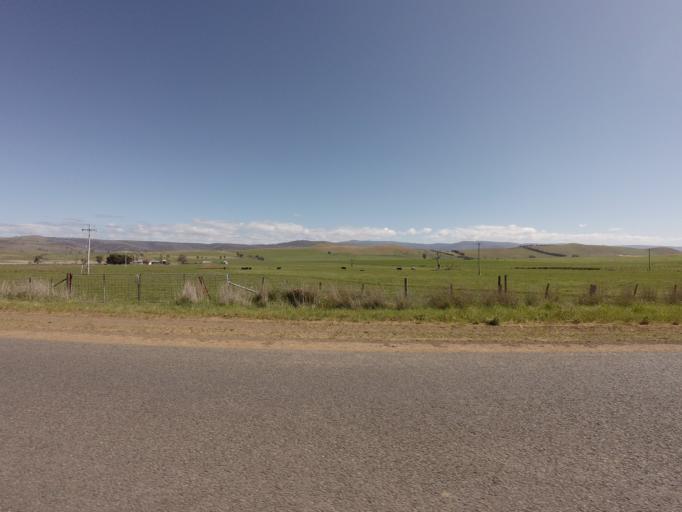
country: AU
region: Tasmania
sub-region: Derwent Valley
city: New Norfolk
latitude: -42.5572
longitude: 146.8074
